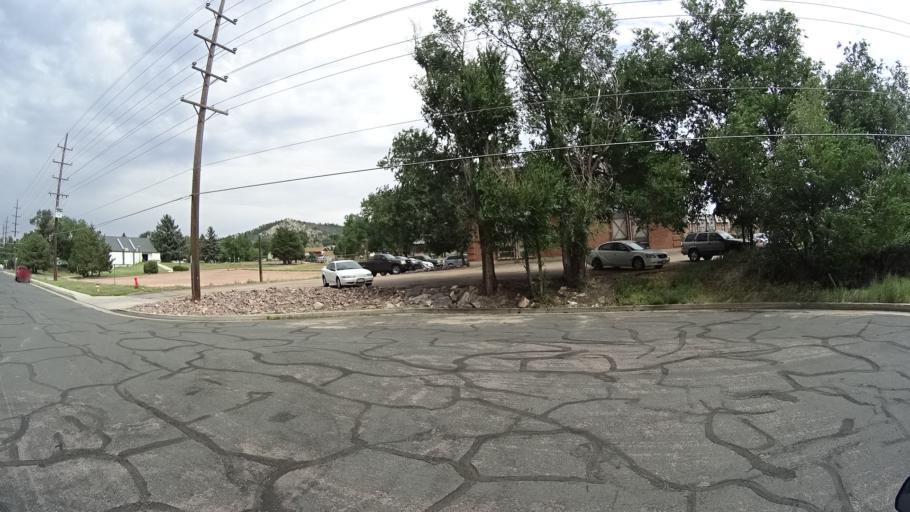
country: US
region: Colorado
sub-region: El Paso County
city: Colorado Springs
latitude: 38.8881
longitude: -104.8128
